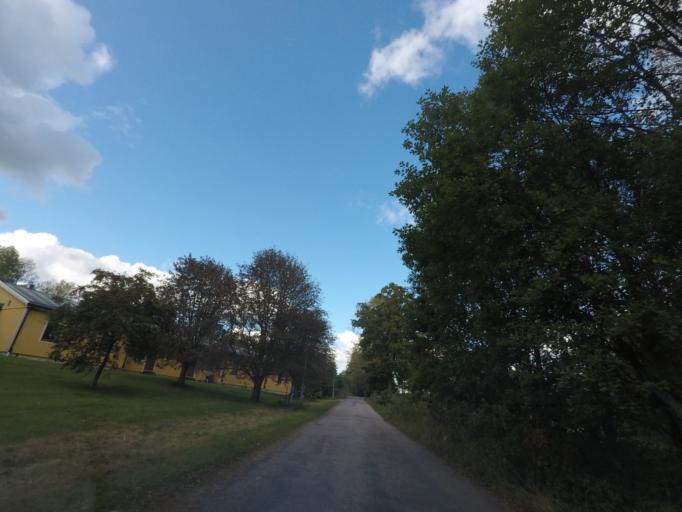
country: SE
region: Vaestmanland
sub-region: Skinnskattebergs Kommun
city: Skinnskatteberg
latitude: 59.8281
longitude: 15.6768
